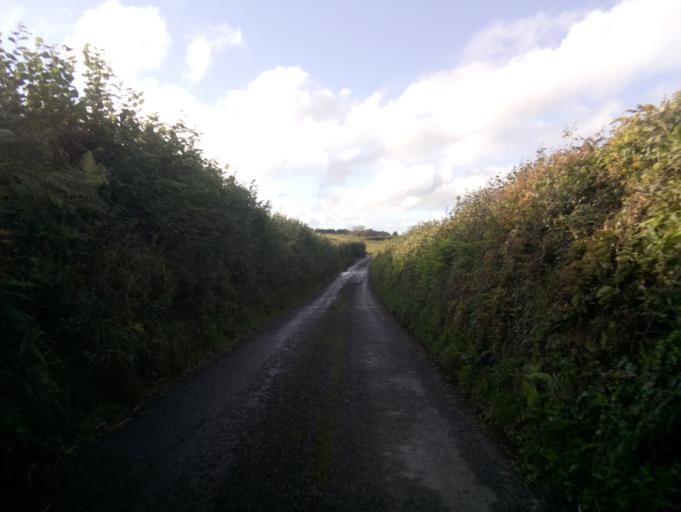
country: GB
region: England
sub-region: Devon
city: Dartmouth
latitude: 50.3440
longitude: -3.6103
